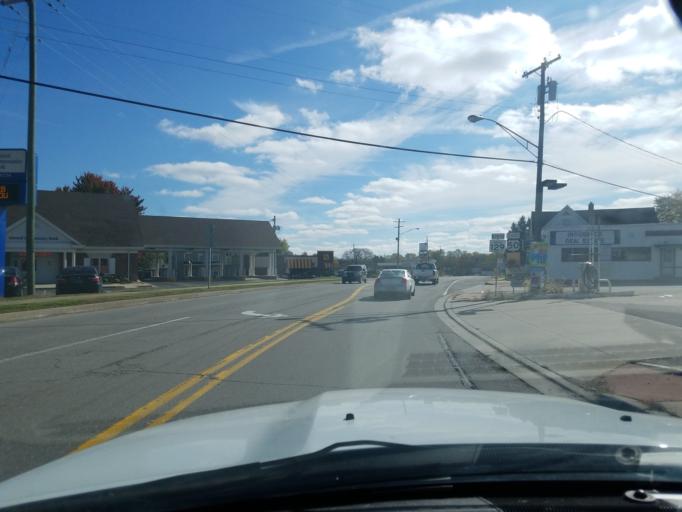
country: US
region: Indiana
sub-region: Ripley County
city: Versailles
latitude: 39.0696
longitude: -85.2536
